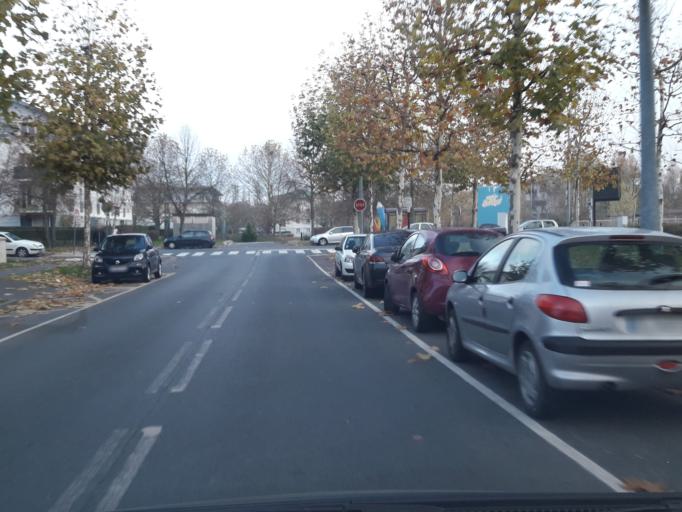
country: FR
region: Ile-de-France
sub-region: Departement de l'Essonne
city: Fleury-Merogis
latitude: 48.6393
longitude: 2.3502
